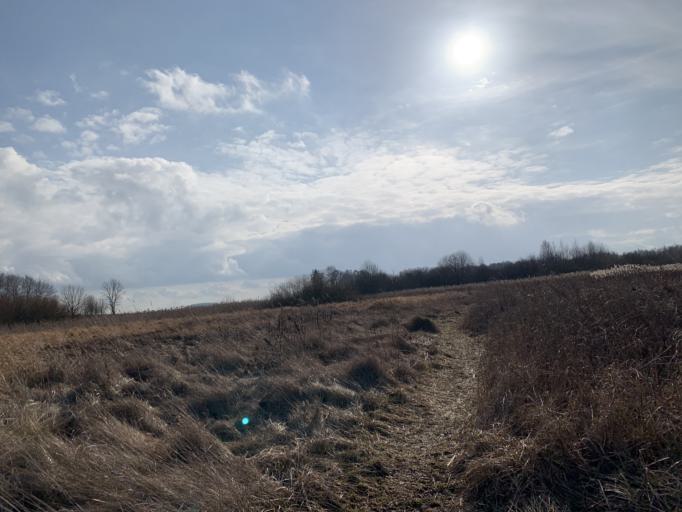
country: BY
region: Minsk
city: Nyasvizh
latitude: 53.2326
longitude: 26.7088
